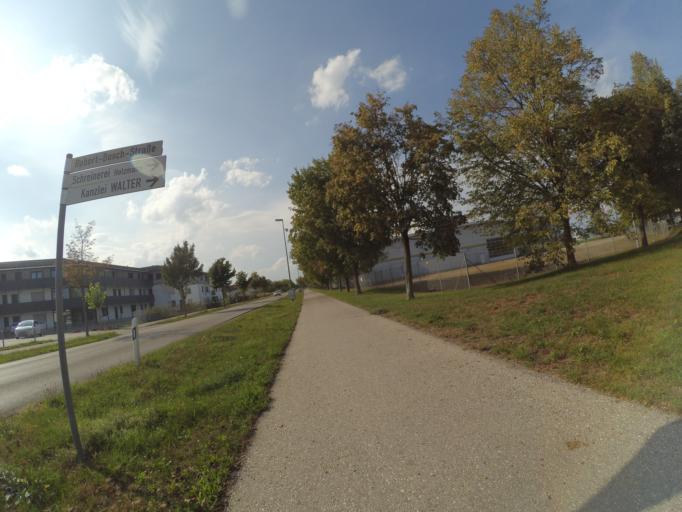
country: DE
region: Bavaria
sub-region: Swabia
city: Buchloe
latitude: 48.0395
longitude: 10.7113
